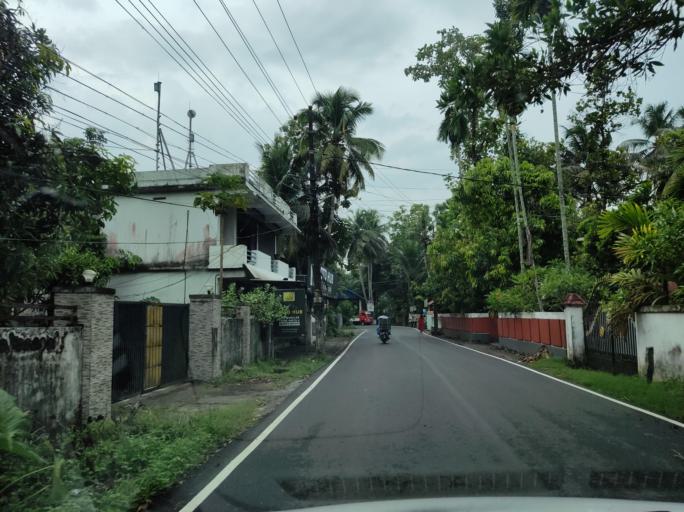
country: IN
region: Kerala
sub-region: Alappuzha
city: Kayankulam
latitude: 9.2618
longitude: 76.4083
